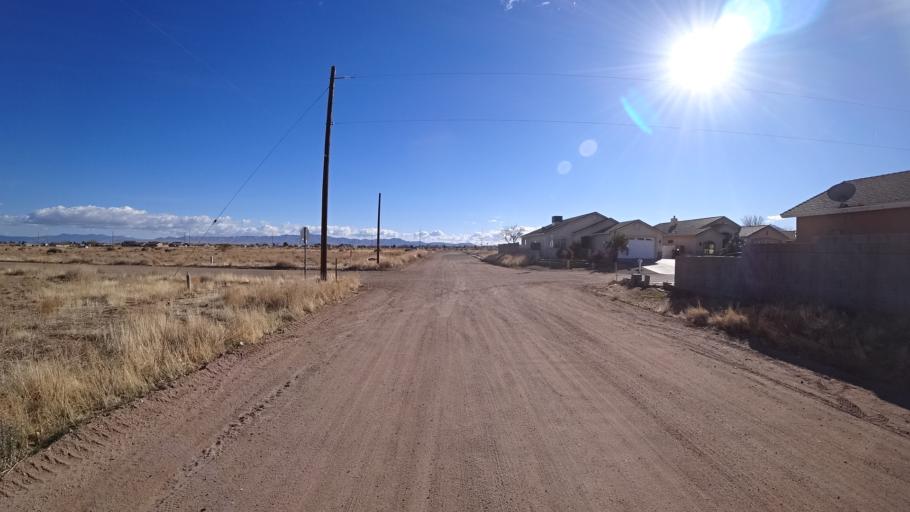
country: US
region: Arizona
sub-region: Mohave County
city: New Kingman-Butler
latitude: 35.2282
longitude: -114.0140
